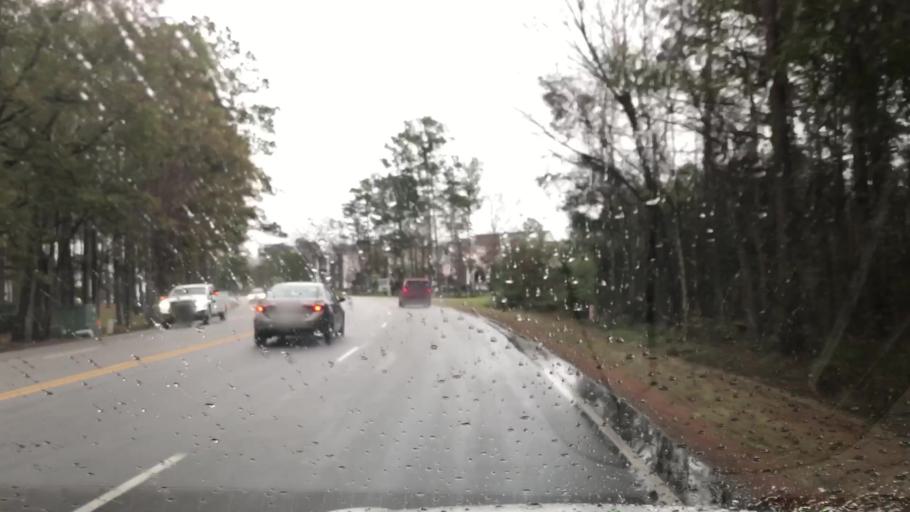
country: US
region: South Carolina
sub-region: Horry County
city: Forestbrook
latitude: 33.7212
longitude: -78.9242
